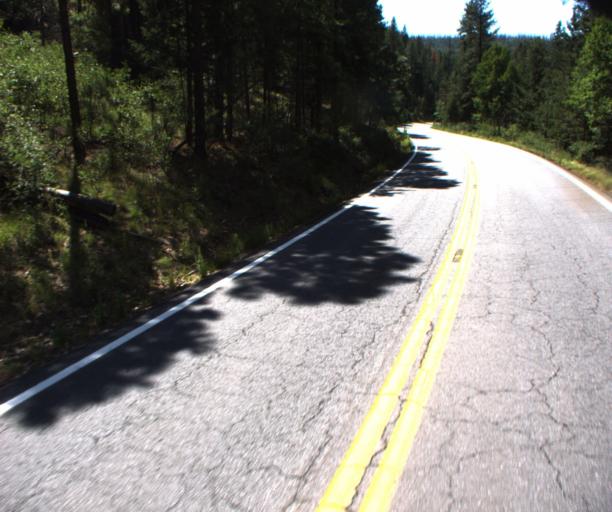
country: US
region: Arizona
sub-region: Apache County
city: Eagar
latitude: 33.8115
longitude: -109.1585
